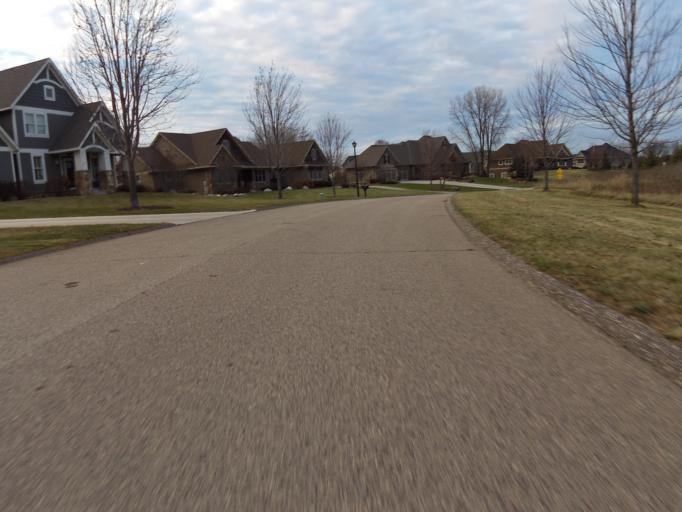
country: US
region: Minnesota
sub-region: Washington County
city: Bayport
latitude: 44.9980
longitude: -92.7961
